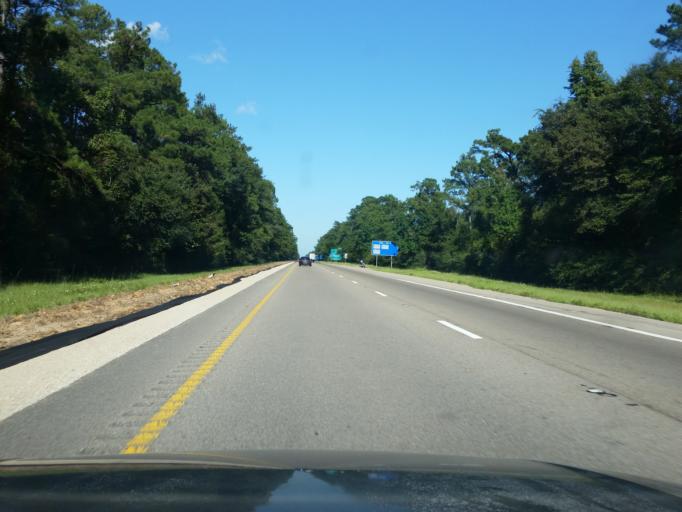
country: US
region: Mississippi
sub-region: Hancock County
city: Pearlington
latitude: 30.3082
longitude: -89.6217
